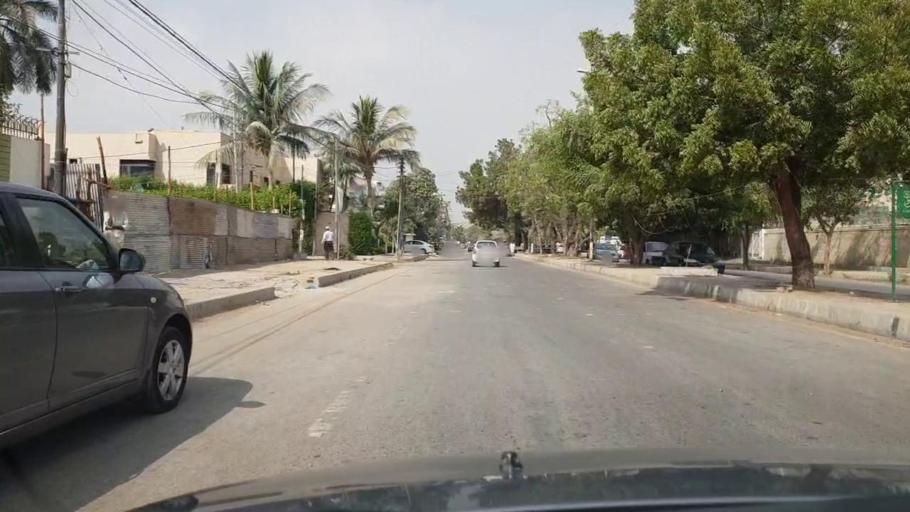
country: PK
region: Sindh
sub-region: Karachi District
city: Karachi
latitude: 24.8722
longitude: 67.0882
